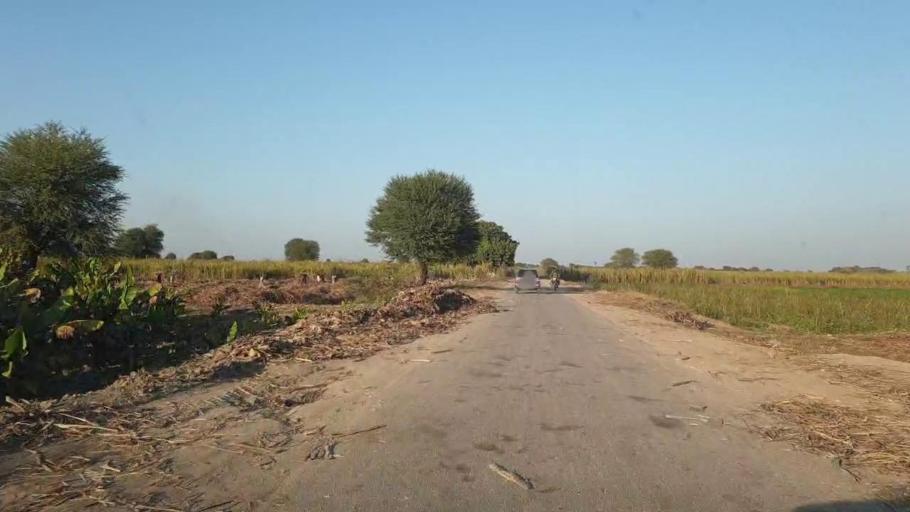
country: PK
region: Sindh
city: Chambar
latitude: 25.3591
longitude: 68.7389
